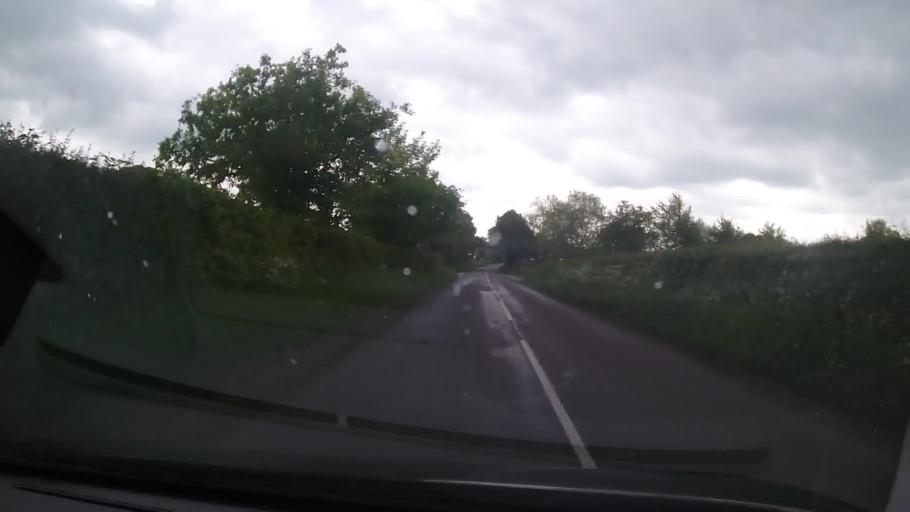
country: GB
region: England
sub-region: Shropshire
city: Petton
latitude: 52.8767
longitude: -2.7835
